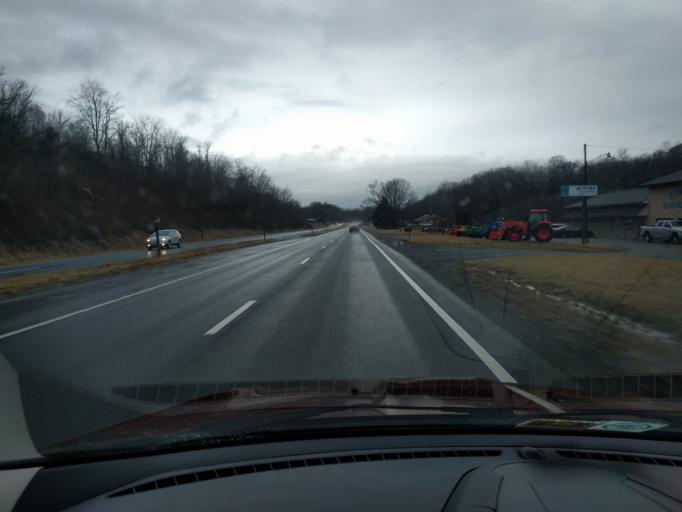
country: US
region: Virginia
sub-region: Giles County
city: Pembroke
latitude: 37.3013
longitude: -80.5516
